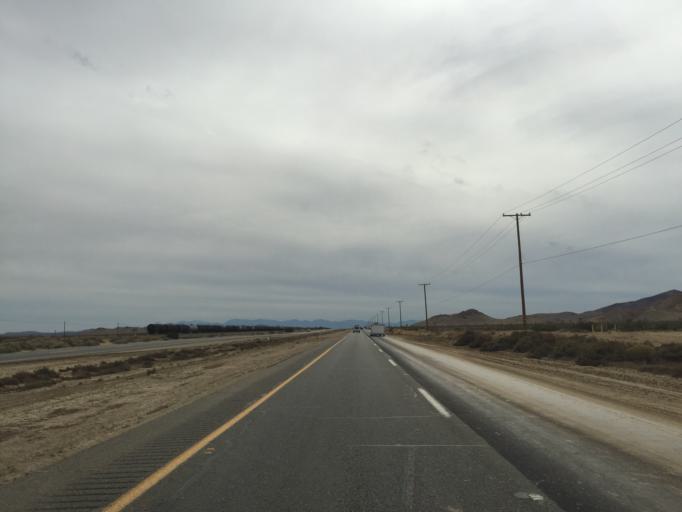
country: US
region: California
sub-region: Kern County
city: Mojave
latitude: 35.0228
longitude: -118.1653
